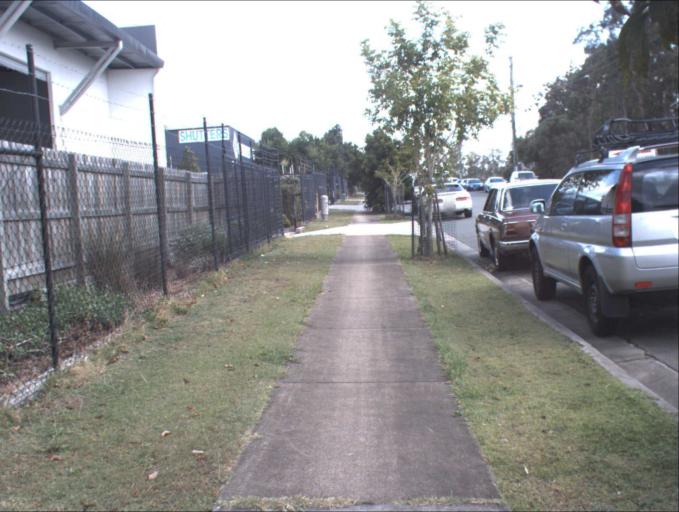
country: AU
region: Queensland
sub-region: Logan
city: Slacks Creek
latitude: -27.6632
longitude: 153.1333
